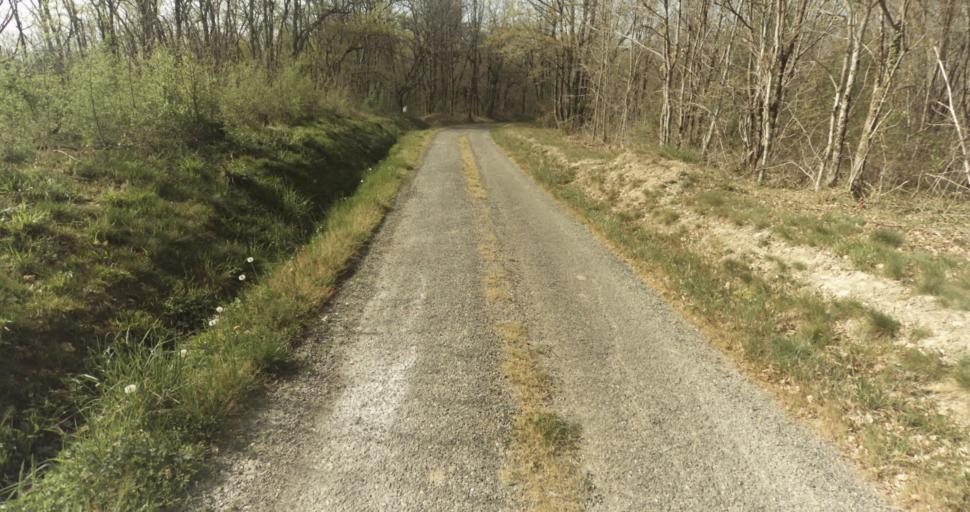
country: FR
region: Midi-Pyrenees
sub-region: Departement du Tarn-et-Garonne
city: Lafrancaise
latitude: 44.1519
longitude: 1.1770
